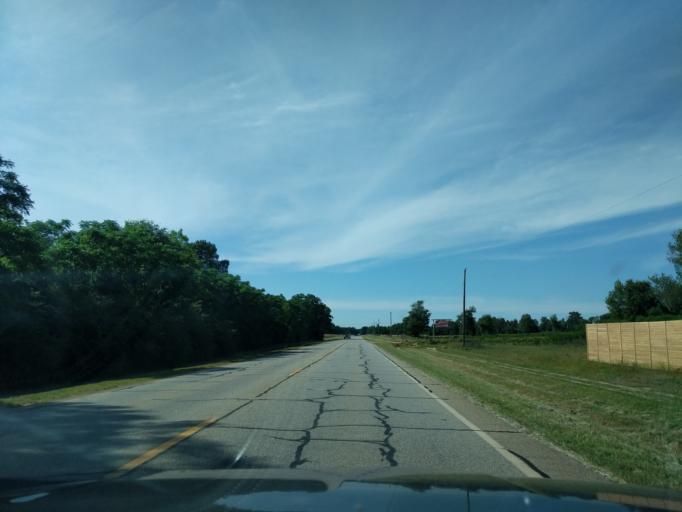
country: US
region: Georgia
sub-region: Jefferson County
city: Wrens
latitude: 33.2275
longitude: -82.3804
